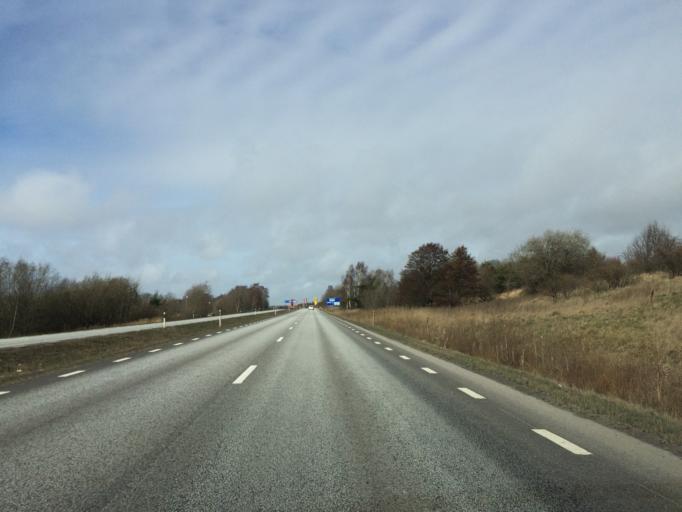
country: SE
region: Halland
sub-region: Halmstads Kommun
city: Fyllinge
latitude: 56.6456
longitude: 12.9191
